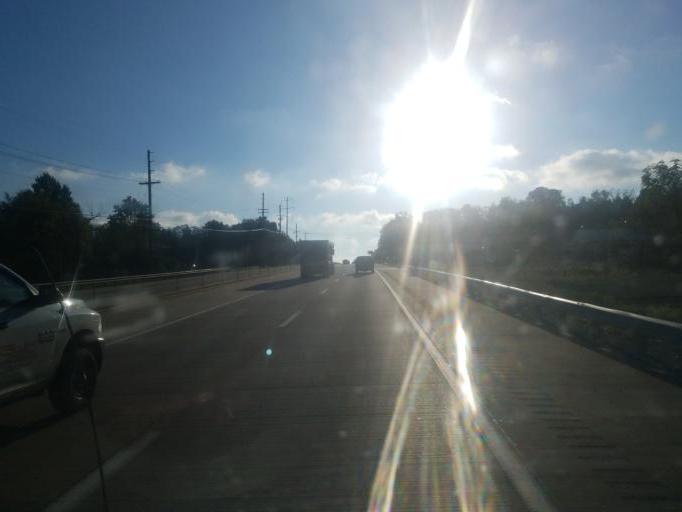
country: US
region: Pennsylvania
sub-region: Westmoreland County
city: Delmont
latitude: 40.4028
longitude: -79.5947
